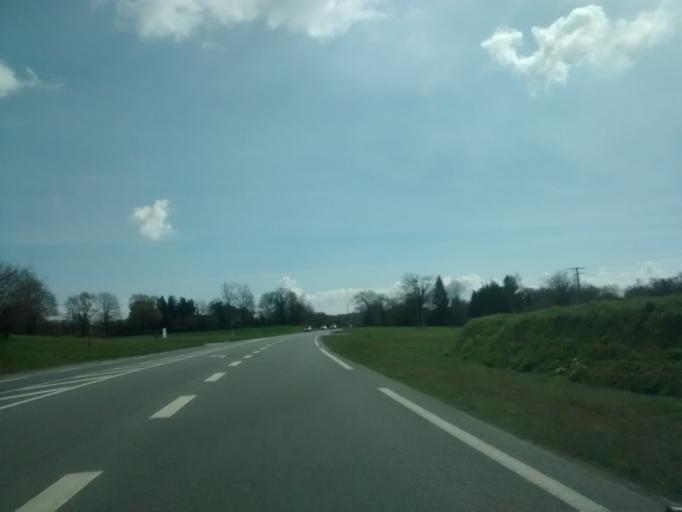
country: FR
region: Brittany
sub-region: Departement d'Ille-et-Vilaine
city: Vern-sur-Seiche
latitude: 48.0747
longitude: -1.5795
